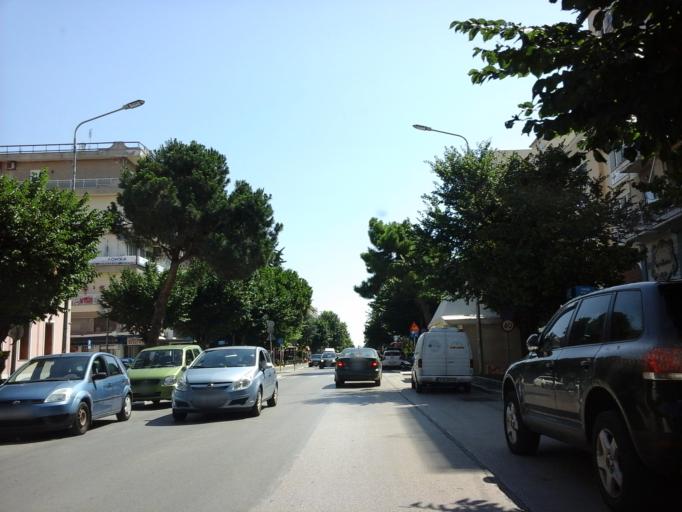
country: GR
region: East Macedonia and Thrace
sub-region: Nomos Evrou
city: Alexandroupoli
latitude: 40.8444
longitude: 25.8729
